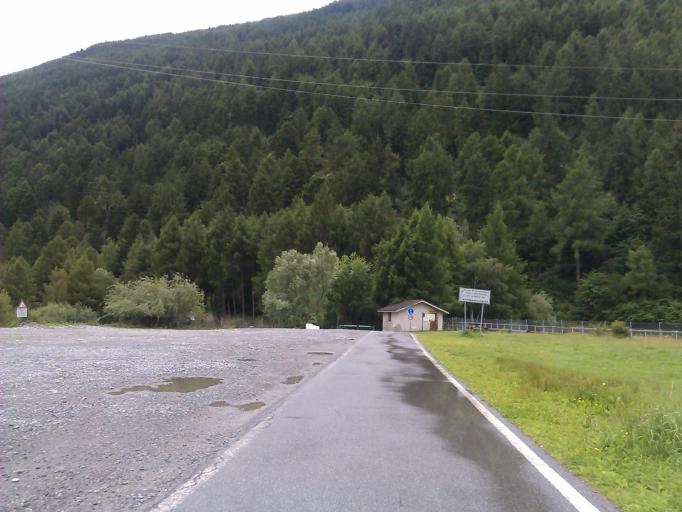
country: IT
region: Trentino-Alto Adige
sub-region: Bolzano
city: Lasa
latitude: 46.6117
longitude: 10.7094
